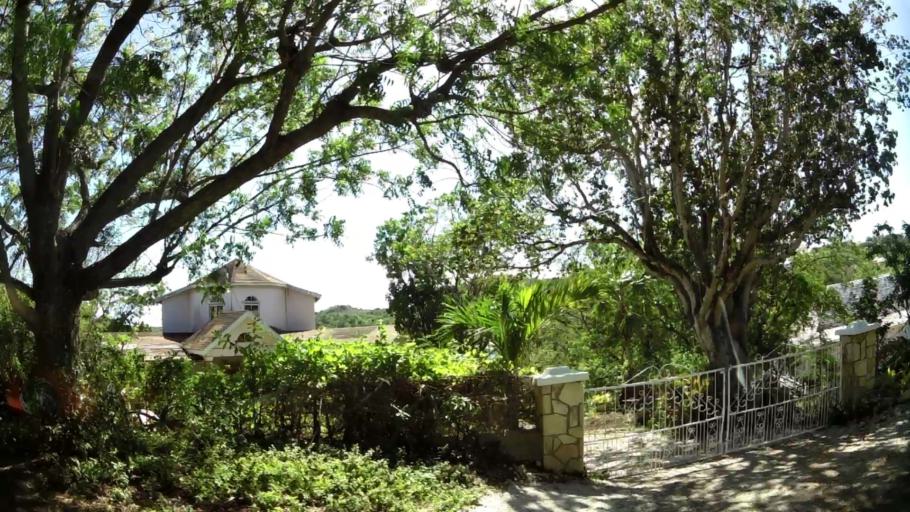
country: AG
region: Saint Paul
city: Falmouth
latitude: 17.0124
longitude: -61.7669
